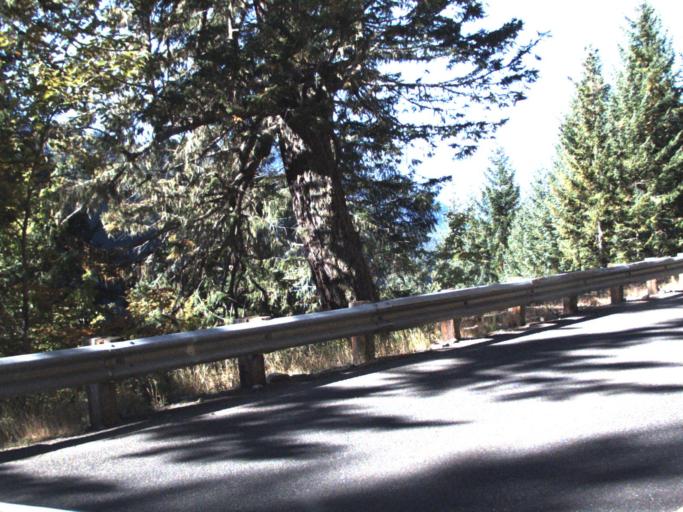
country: US
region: Washington
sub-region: Yakima County
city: Tieton
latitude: 46.6657
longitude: -121.4840
